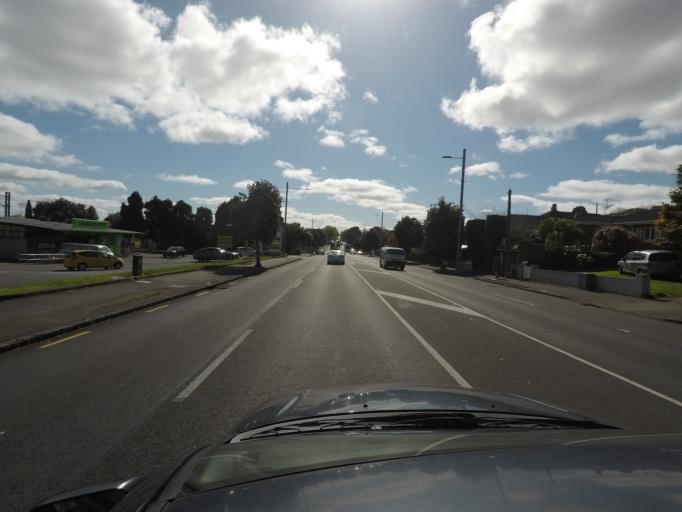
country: NZ
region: Auckland
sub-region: Auckland
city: Rosebank
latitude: -36.8879
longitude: 174.7116
